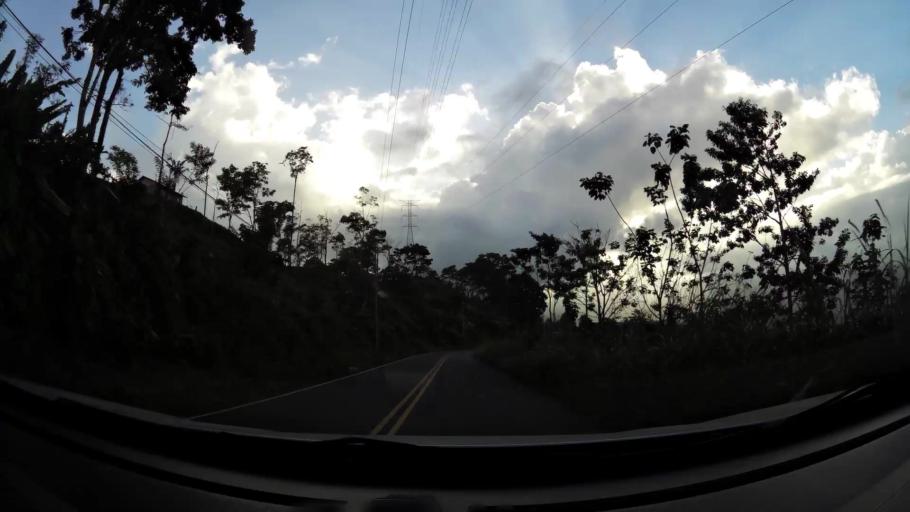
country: CR
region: Limon
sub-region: Canton de Siquirres
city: Siquirres
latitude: 10.0054
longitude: -83.5711
